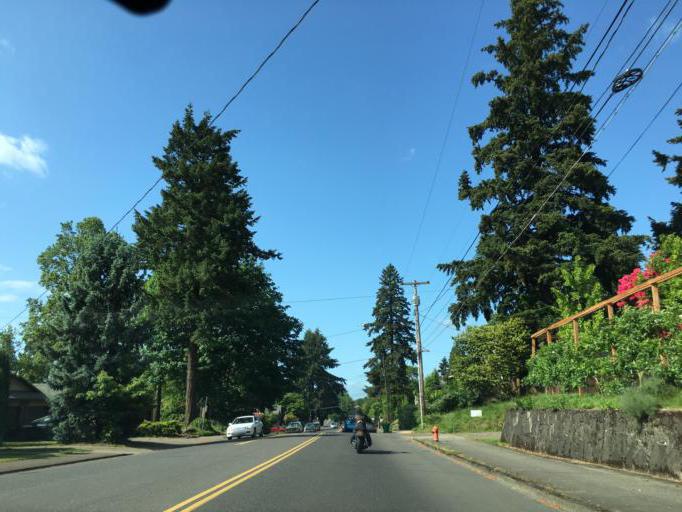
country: US
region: Oregon
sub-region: Clackamas County
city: Milwaukie
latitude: 45.4851
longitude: -122.6226
